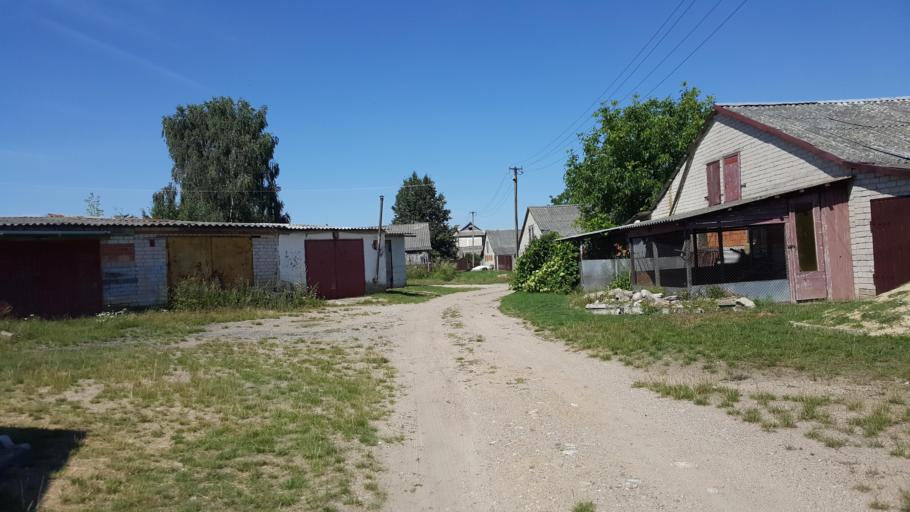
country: BY
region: Brest
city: Charnawchytsy
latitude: 52.2651
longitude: 23.5950
